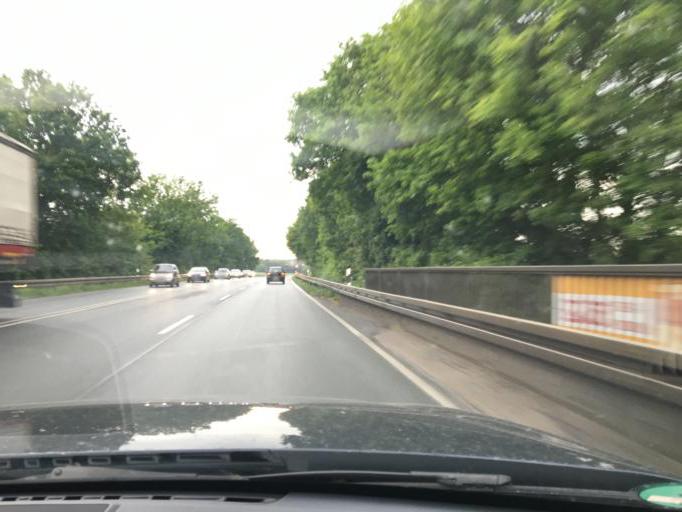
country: DE
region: North Rhine-Westphalia
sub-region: Regierungsbezirk Munster
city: Greven
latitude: 52.1113
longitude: 7.6123
